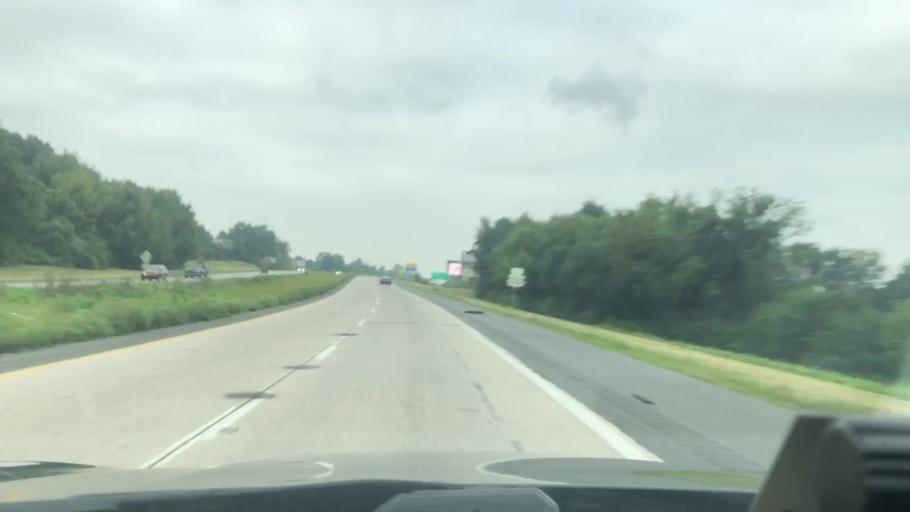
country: US
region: Pennsylvania
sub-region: Berks County
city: Temple
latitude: 40.4280
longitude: -75.9167
